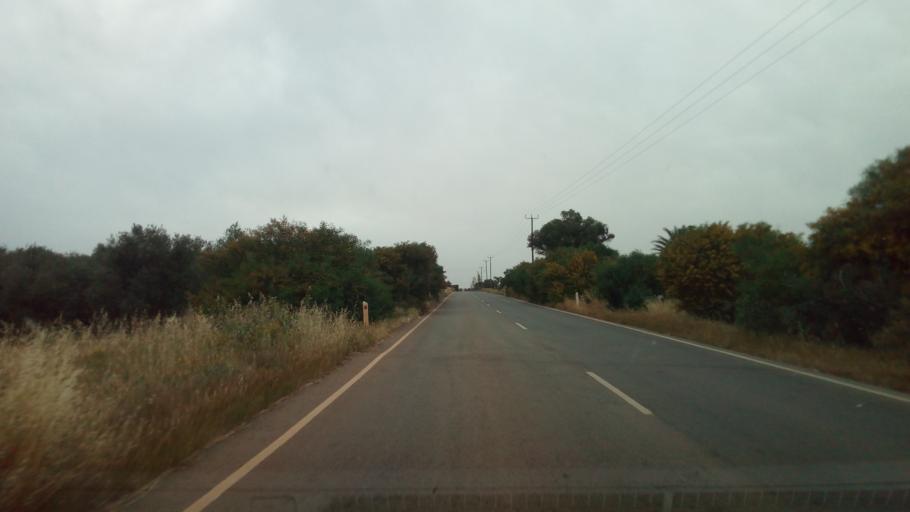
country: CY
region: Ammochostos
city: Liopetri
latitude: 34.9756
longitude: 33.8684
